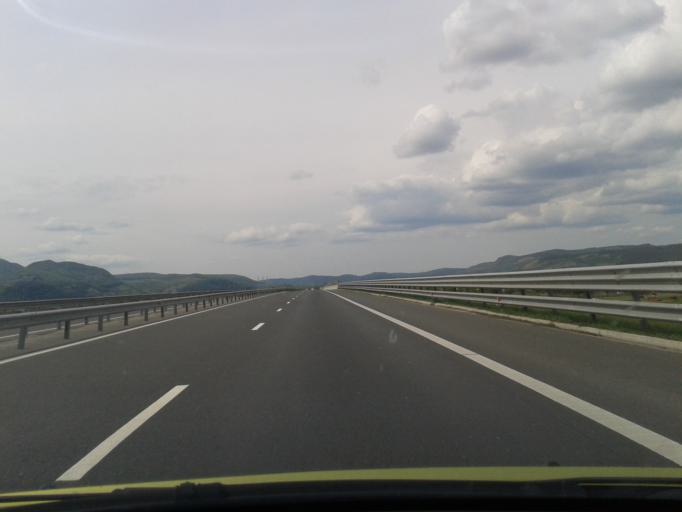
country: RO
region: Hunedoara
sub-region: Comuna Harau
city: Harau
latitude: 45.8917
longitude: 22.9567
